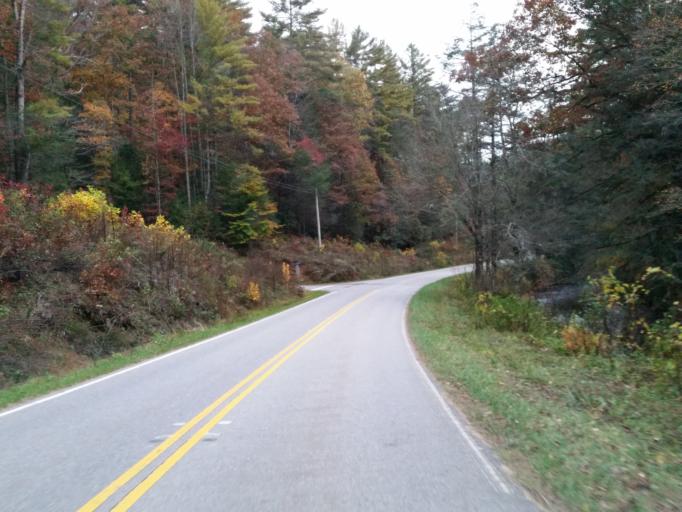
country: US
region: Georgia
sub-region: Union County
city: Blairsville
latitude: 34.7402
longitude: -84.0868
